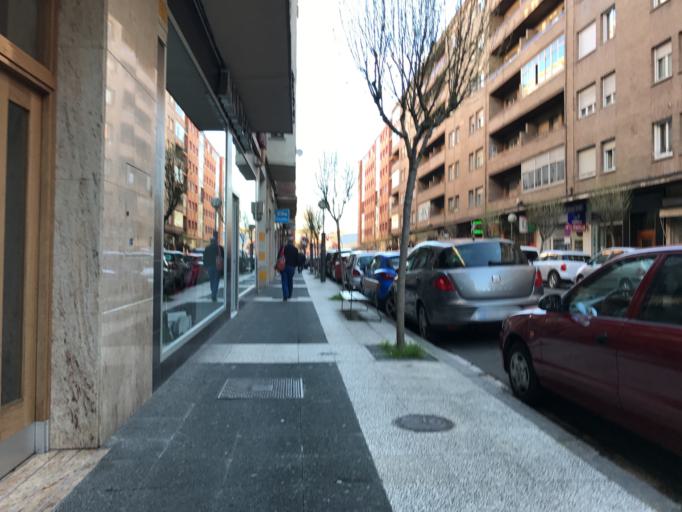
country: ES
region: Basque Country
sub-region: Provincia de Alava
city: Gasteiz / Vitoria
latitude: 42.8551
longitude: -2.6762
